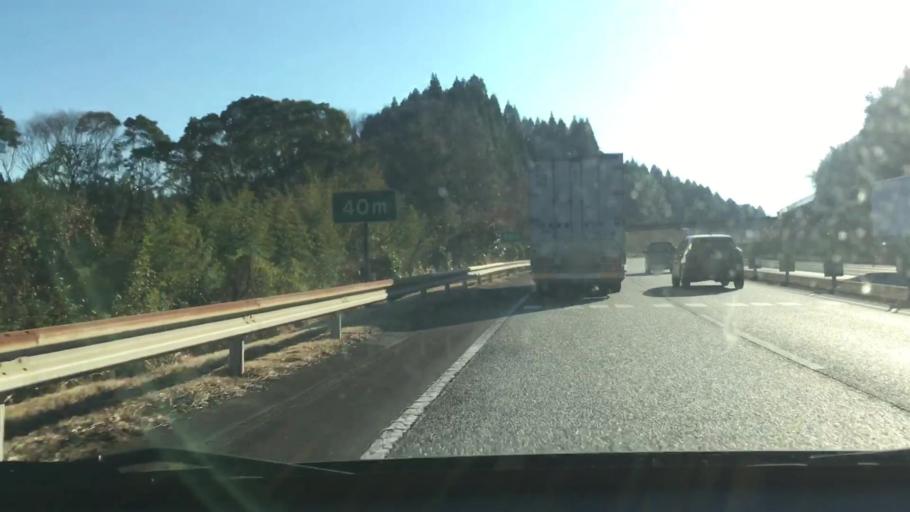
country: JP
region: Kagoshima
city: Kajiki
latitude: 31.8736
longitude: 130.6940
